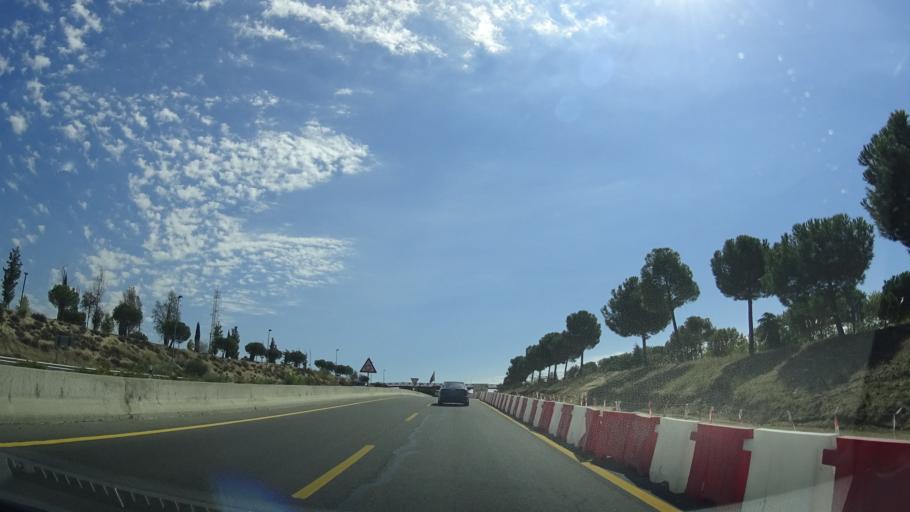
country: ES
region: Madrid
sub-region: Provincia de Madrid
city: Boadilla del Monte
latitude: 40.4115
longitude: -3.8842
